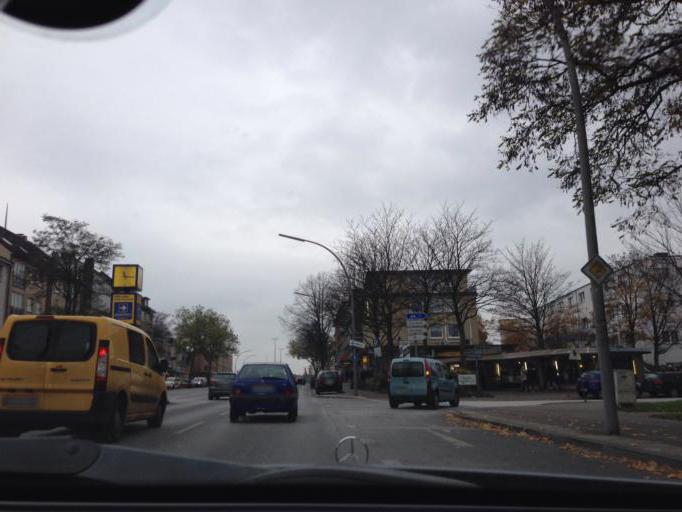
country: DE
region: Hamburg
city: Marienthal
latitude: 53.5743
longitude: 10.0738
